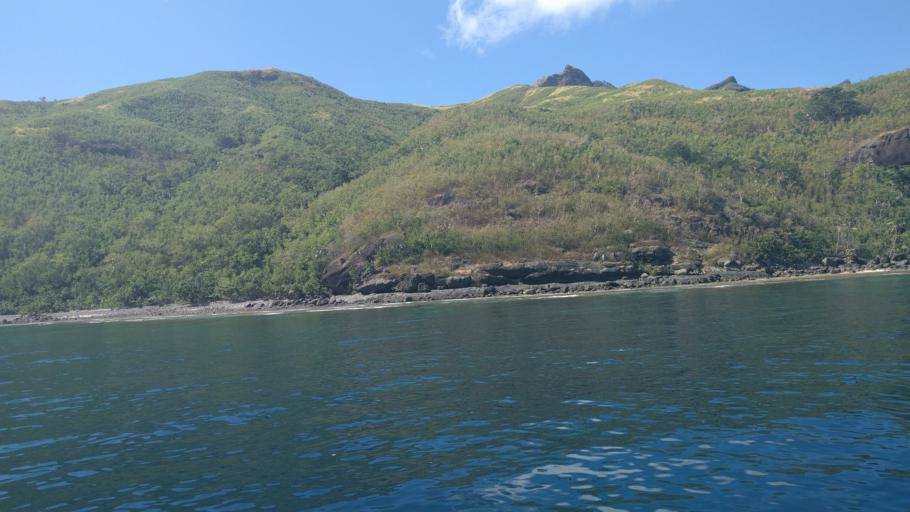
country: FJ
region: Western
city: Lautoka
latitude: -17.2849
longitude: 177.1024
